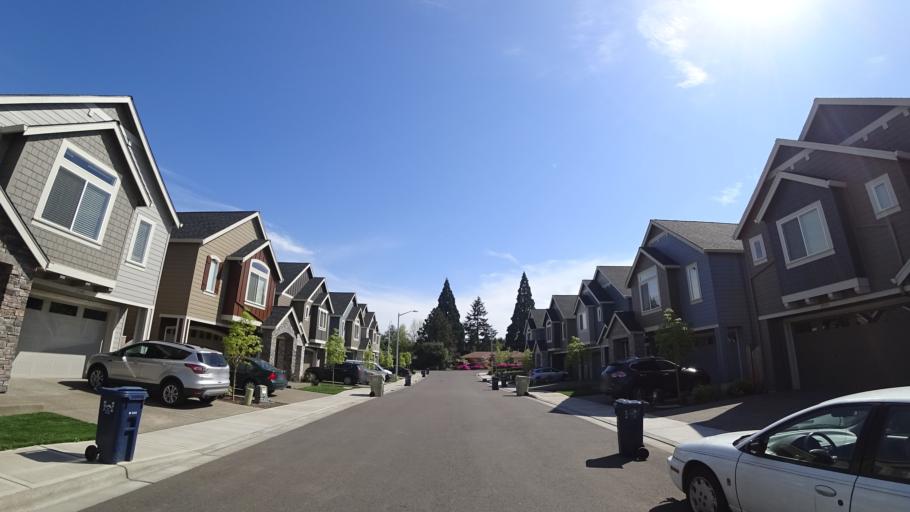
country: US
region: Oregon
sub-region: Washington County
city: Aloha
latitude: 45.5012
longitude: -122.8894
